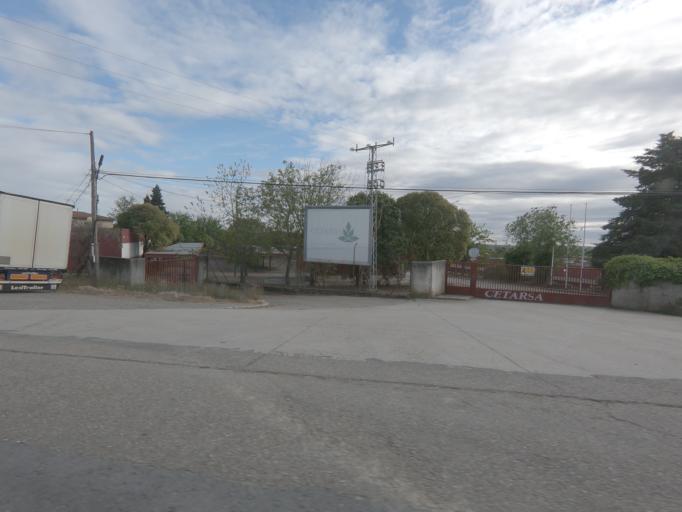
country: ES
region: Extremadura
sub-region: Provincia de Caceres
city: Coria
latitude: 40.0057
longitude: -6.5556
